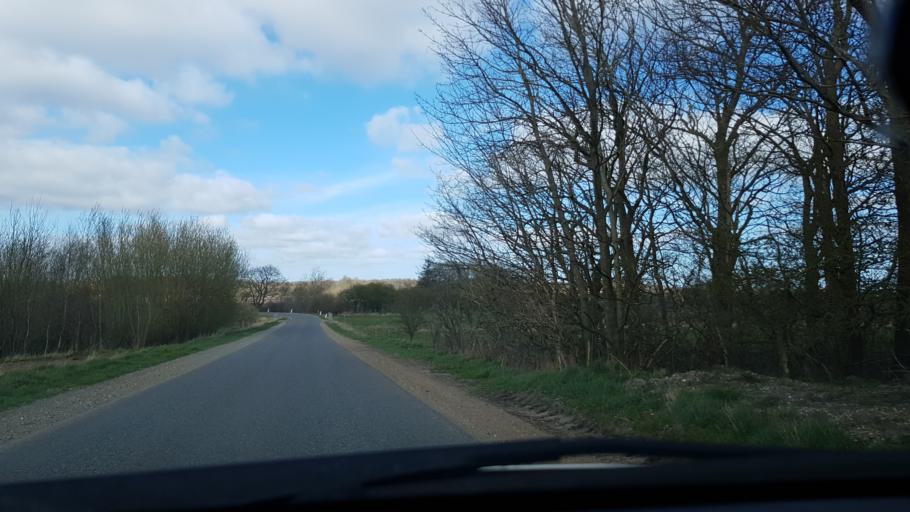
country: DK
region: South Denmark
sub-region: Vejen Kommune
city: Rodding
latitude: 55.3765
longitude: 8.9985
